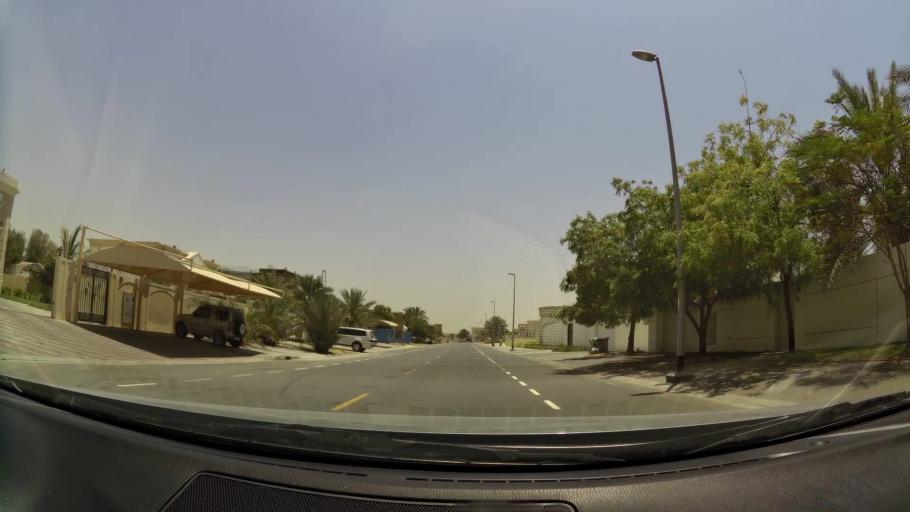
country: AE
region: Dubai
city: Dubai
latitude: 25.0961
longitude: 55.1943
